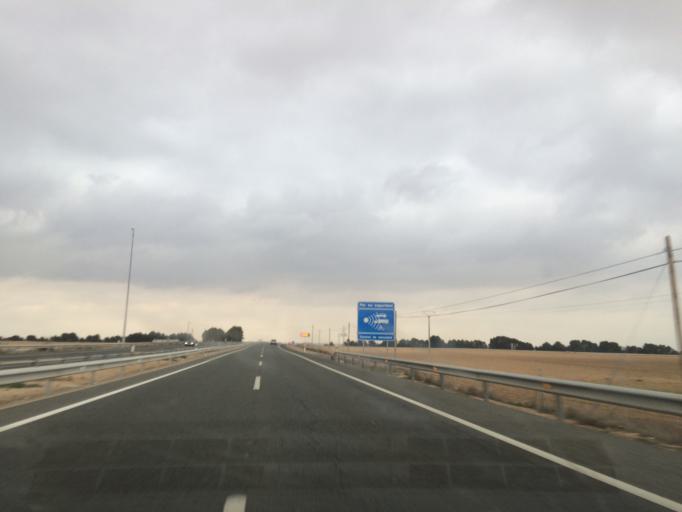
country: ES
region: Castille-La Mancha
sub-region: Province of Toledo
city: Tembleque
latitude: 39.6656
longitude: -3.5116
